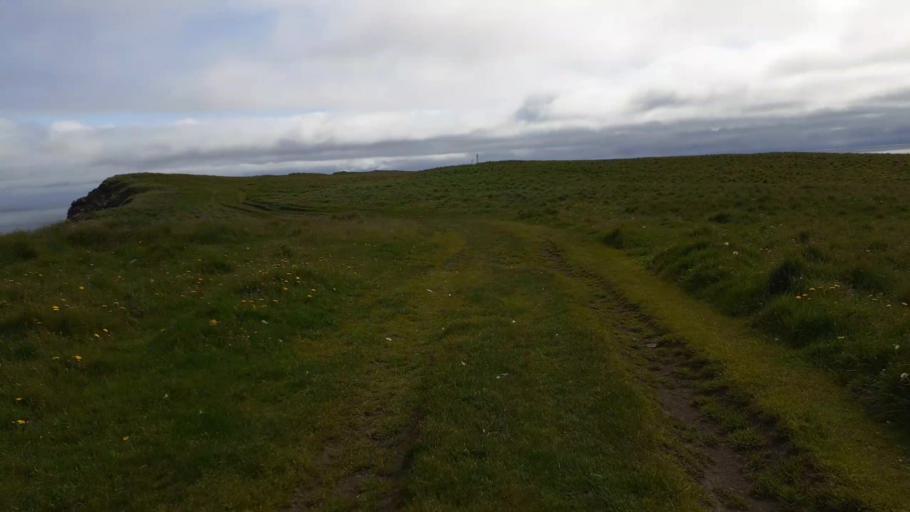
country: IS
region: Northeast
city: Dalvik
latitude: 66.5549
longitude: -18.0016
